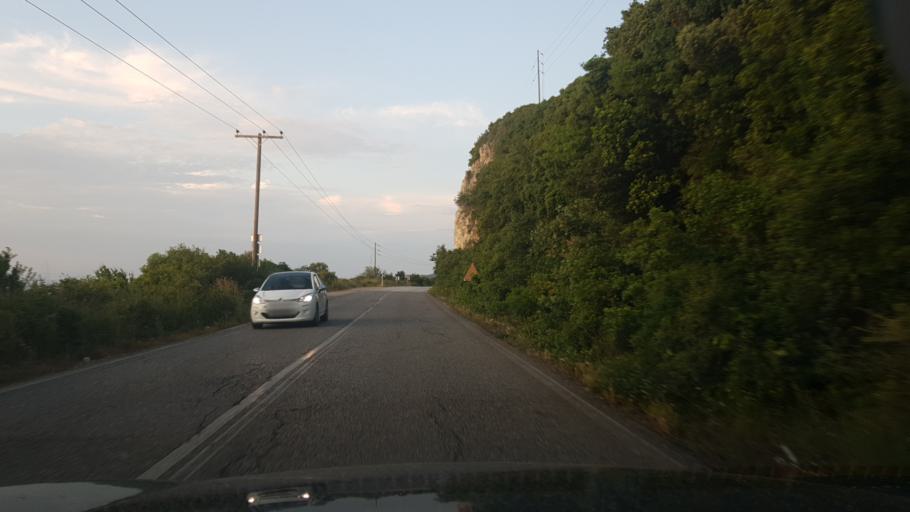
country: GR
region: Ionian Islands
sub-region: Lefkada
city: Lefkada
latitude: 38.8570
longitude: 20.7507
